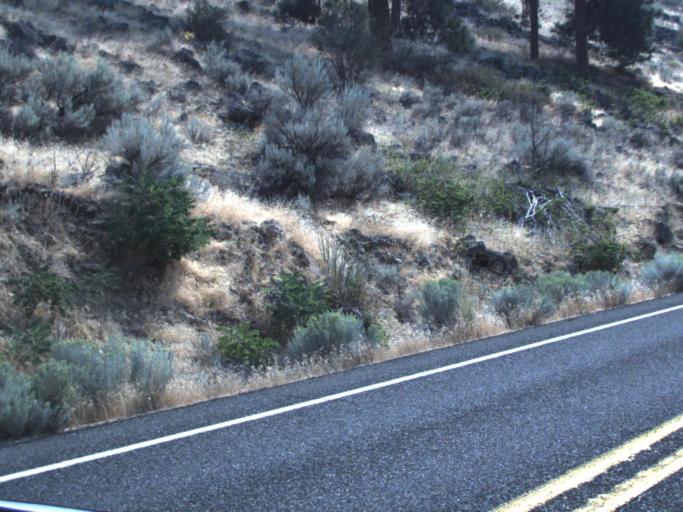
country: US
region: Washington
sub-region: Kittitas County
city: Kittitas
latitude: 46.8803
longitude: -120.4742
